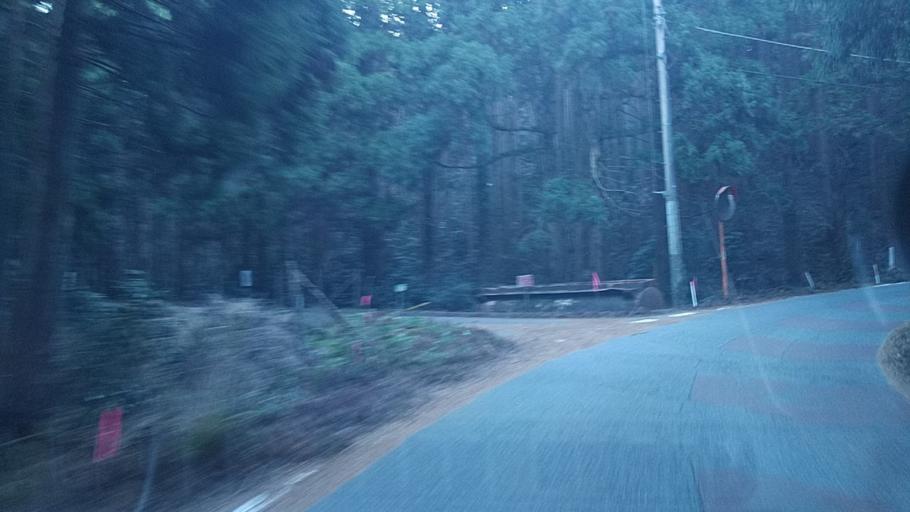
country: JP
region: Chiba
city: Kimitsu
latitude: 35.2585
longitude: 139.9502
